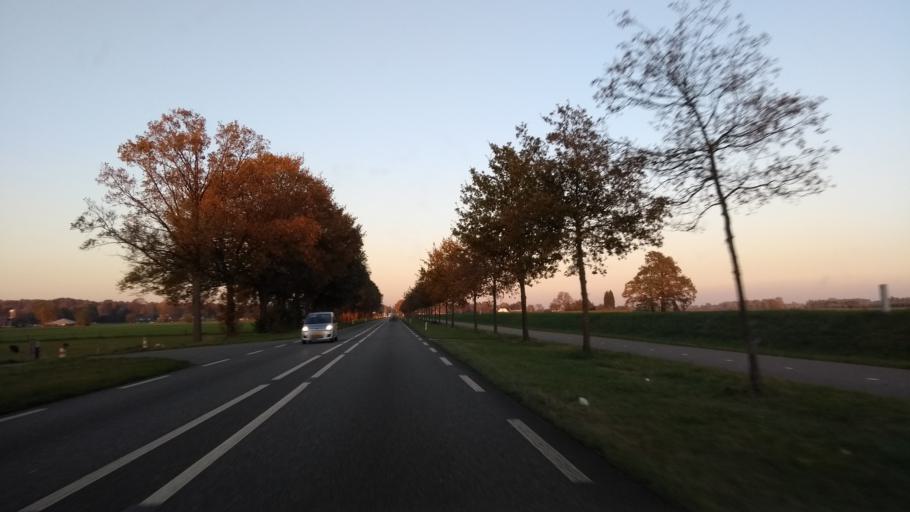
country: NL
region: Gelderland
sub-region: Gemeente Rheden
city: Spankeren
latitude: 52.0679
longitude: 6.1339
